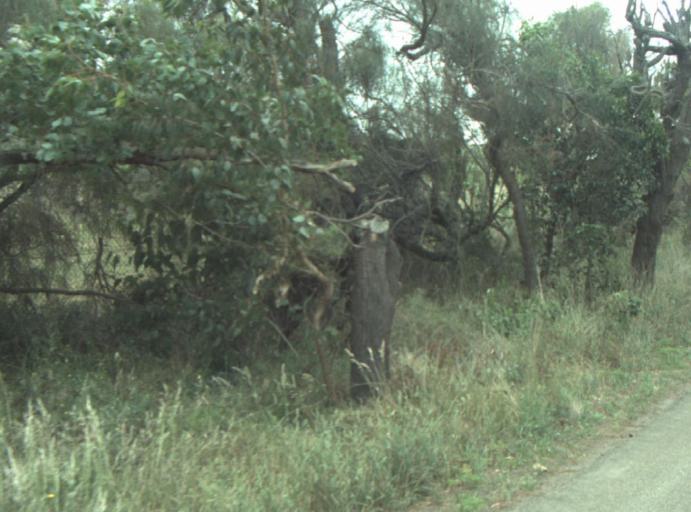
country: AU
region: Victoria
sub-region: Greater Geelong
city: Leopold
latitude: -38.2375
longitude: 144.5026
